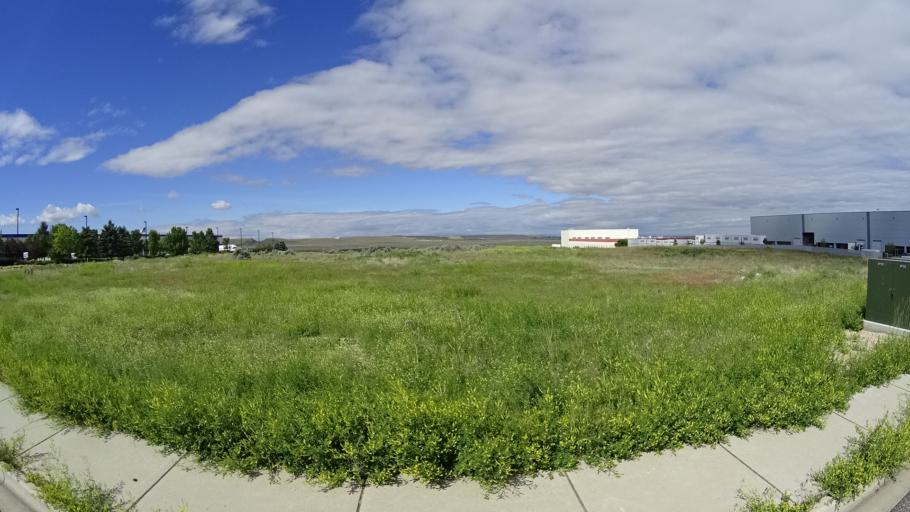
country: US
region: Idaho
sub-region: Ada County
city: Boise
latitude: 43.5389
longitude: -116.1631
